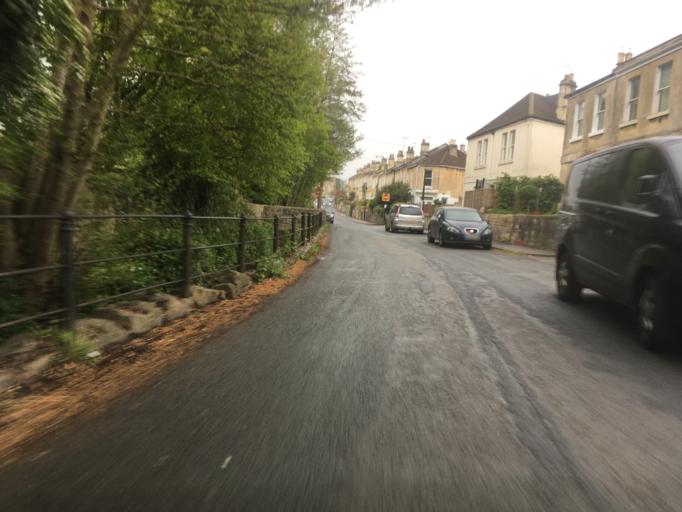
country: GB
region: England
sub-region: Bath and North East Somerset
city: Bath
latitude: 51.4011
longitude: -2.3440
